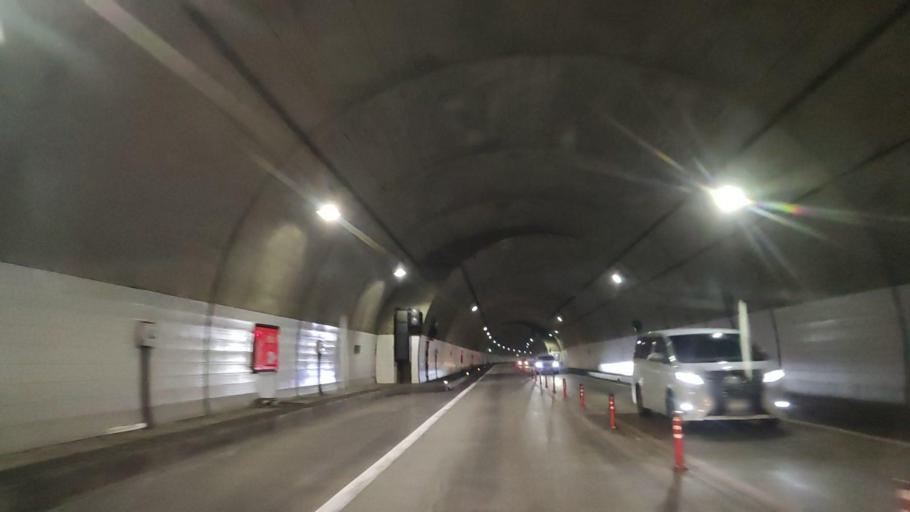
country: JP
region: Akita
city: Odate
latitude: 40.3629
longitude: 140.6960
